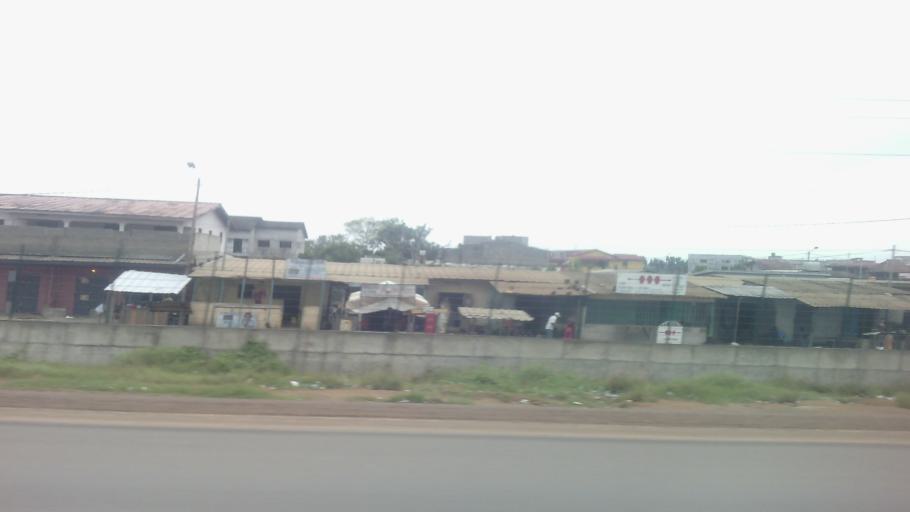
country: CI
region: Lagunes
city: Bingerville
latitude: 5.2392
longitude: -3.8949
